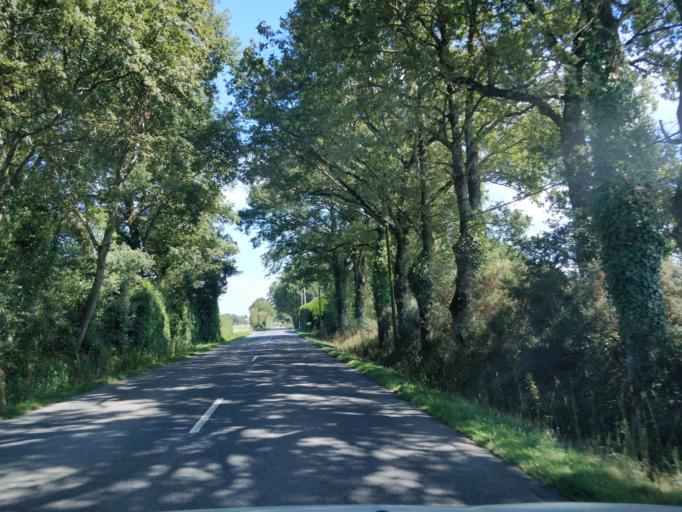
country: FR
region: Pays de la Loire
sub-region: Departement de la Loire-Atlantique
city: Guemene-Penfao
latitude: 47.6403
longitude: -1.8030
